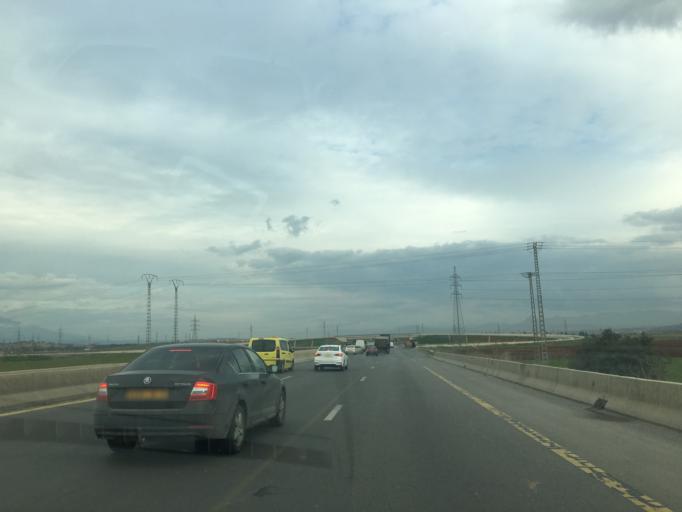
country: DZ
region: Bouira
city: Bouira
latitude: 36.3308
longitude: 3.9393
